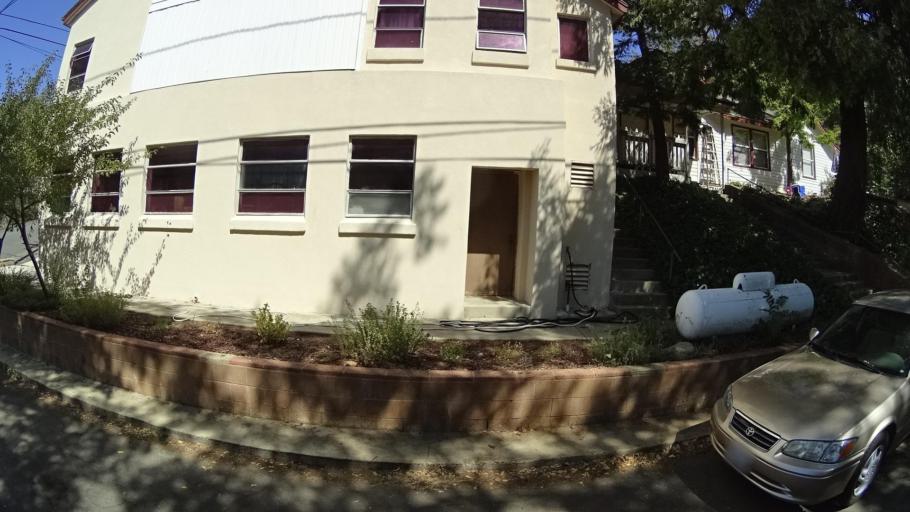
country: US
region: California
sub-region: San Diego County
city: Julian
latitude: 33.0778
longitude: -116.5999
